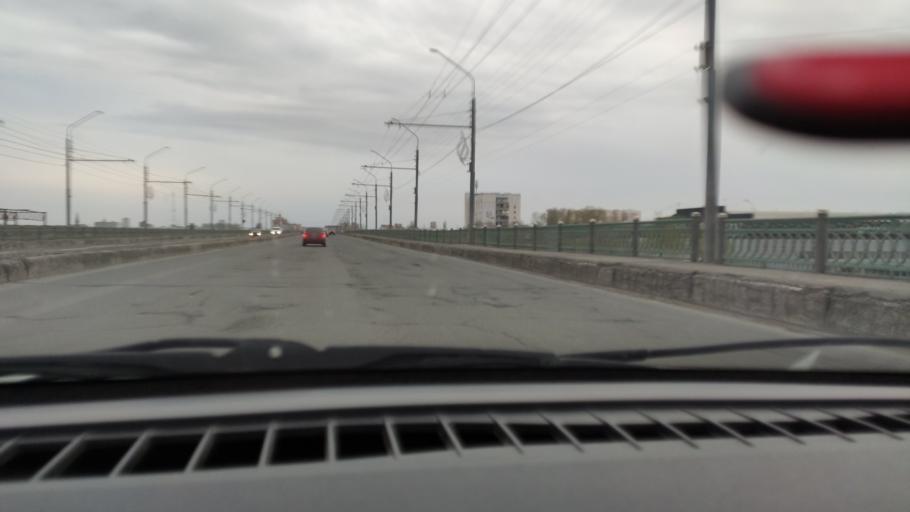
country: RU
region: Orenburg
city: Orenburg
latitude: 51.7999
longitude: 55.1068
